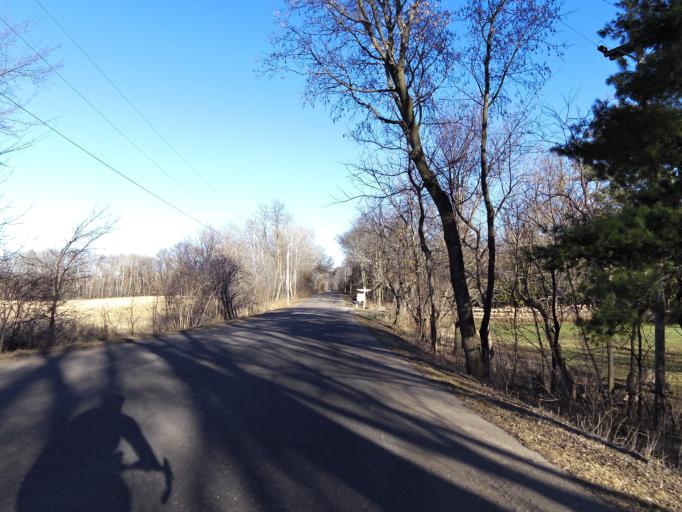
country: US
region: Minnesota
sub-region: Washington County
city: Bayport
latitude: 44.9925
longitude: -92.8111
